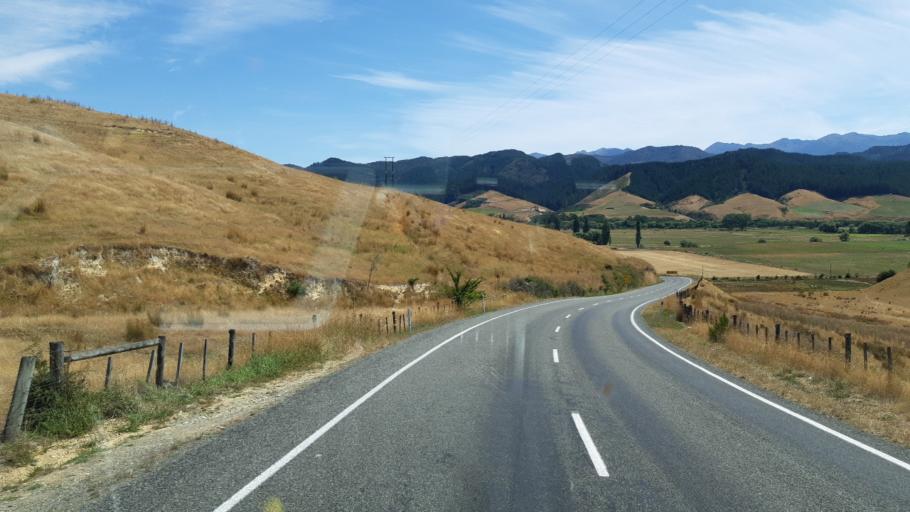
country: NZ
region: Tasman
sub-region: Tasman District
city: Wakefield
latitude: -41.3431
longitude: 172.8125
